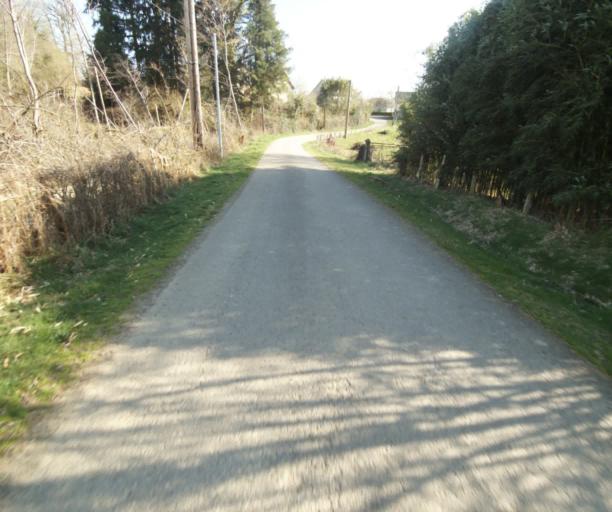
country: FR
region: Limousin
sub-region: Departement de la Correze
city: Saint-Mexant
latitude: 45.3285
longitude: 1.6110
